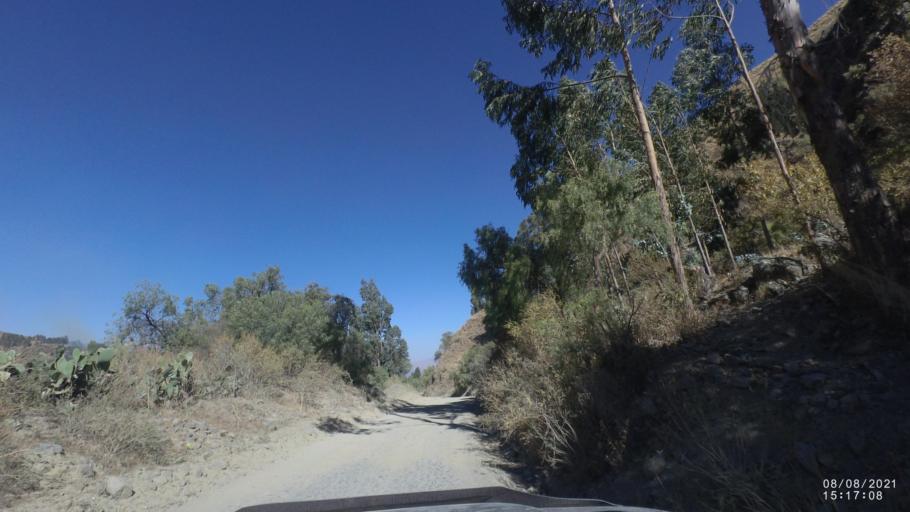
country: BO
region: Cochabamba
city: Cochabamba
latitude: -17.2862
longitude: -66.3047
